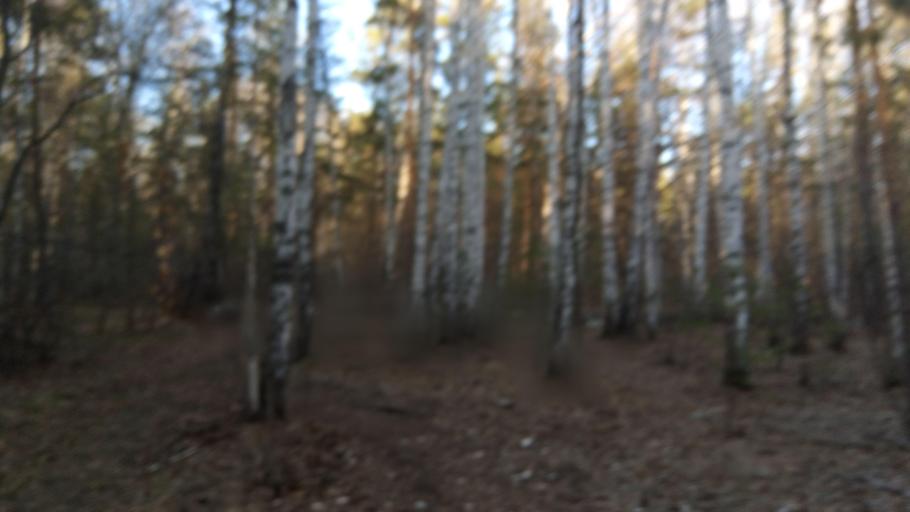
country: RU
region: Chelyabinsk
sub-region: Gorod Chelyabinsk
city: Chelyabinsk
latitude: 55.1435
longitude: 61.3405
